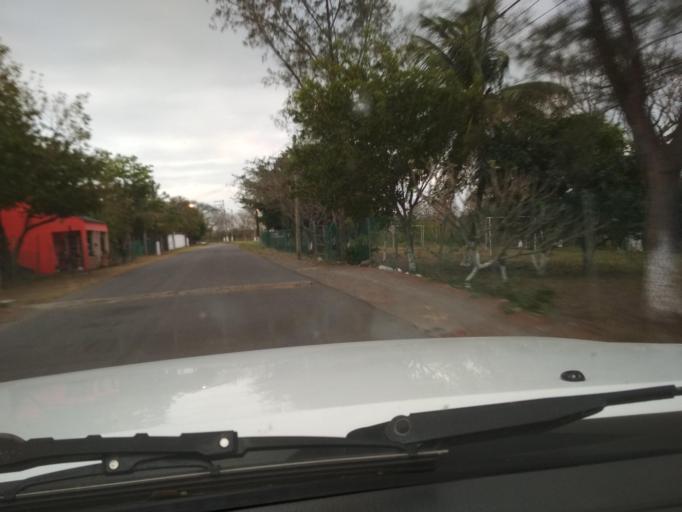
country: MX
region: Veracruz
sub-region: Veracruz
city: Delfino Victoria (Santa Fe)
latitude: 19.1624
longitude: -96.2609
